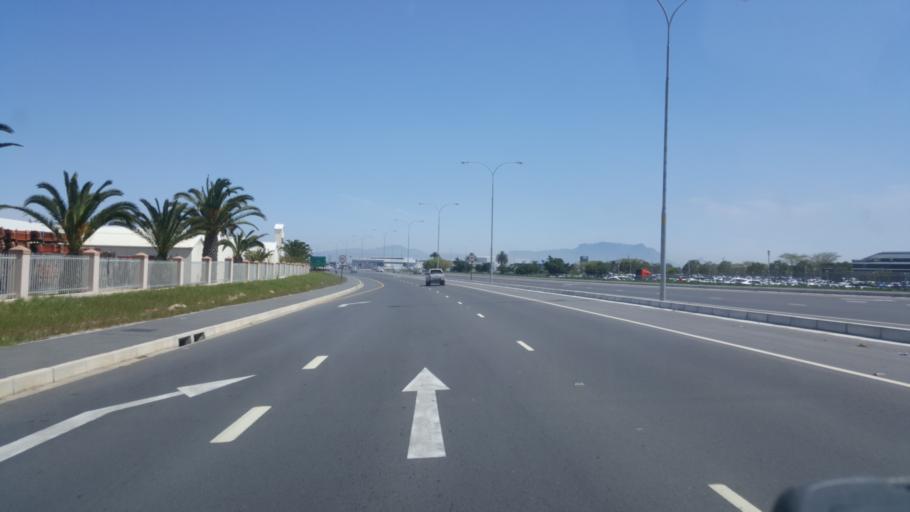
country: ZA
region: Western Cape
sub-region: City of Cape Town
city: Kraaifontein
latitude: -33.9499
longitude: 18.6997
